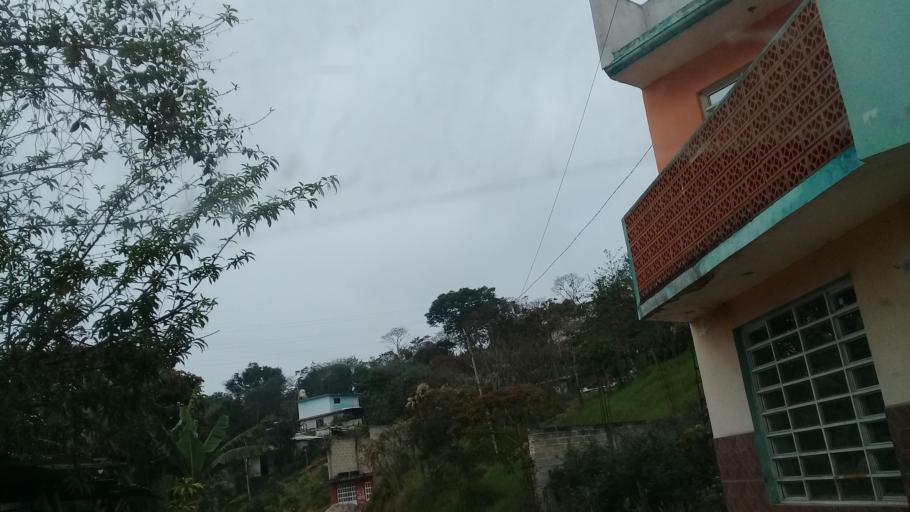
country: MX
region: Veracruz
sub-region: Xalapa
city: Fraccionamiento las Fuentes
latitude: 19.4930
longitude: -96.8988
